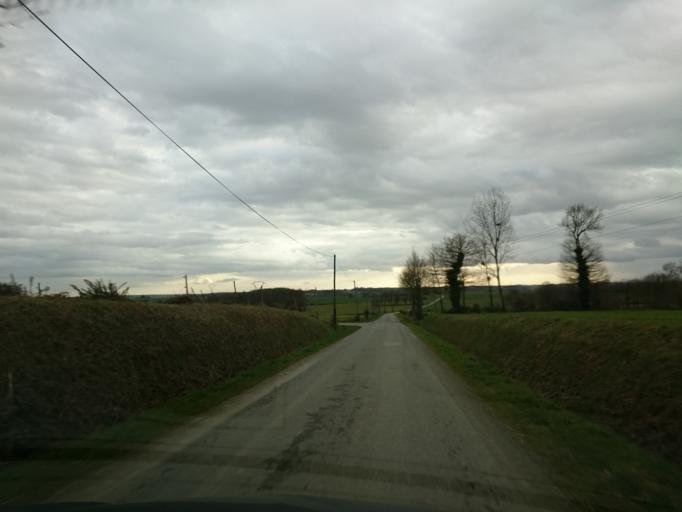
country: FR
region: Brittany
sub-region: Departement d'Ille-et-Vilaine
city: Pance
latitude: 47.9098
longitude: -1.6399
